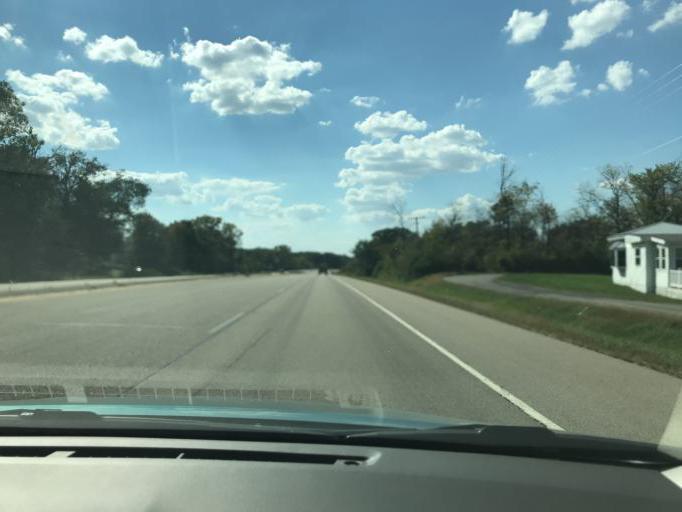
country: US
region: Wisconsin
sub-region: Walworth County
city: Como
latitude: 42.5842
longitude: -88.4941
